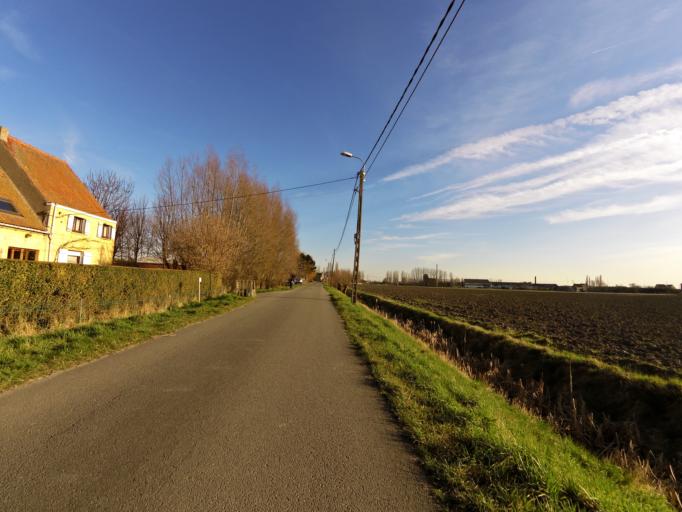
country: BE
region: Flanders
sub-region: Provincie West-Vlaanderen
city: Ostend
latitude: 51.1797
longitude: 2.9137
